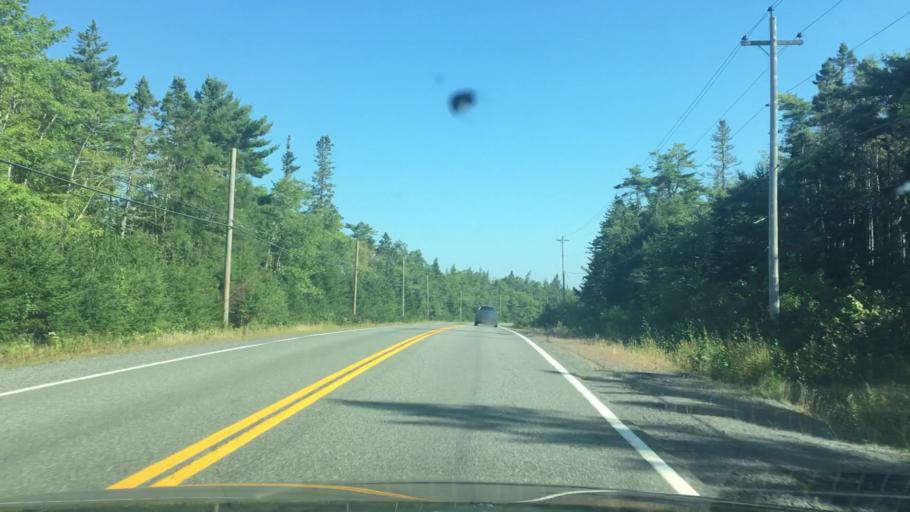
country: CA
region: Nova Scotia
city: Cole Harbour
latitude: 44.7945
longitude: -62.8890
